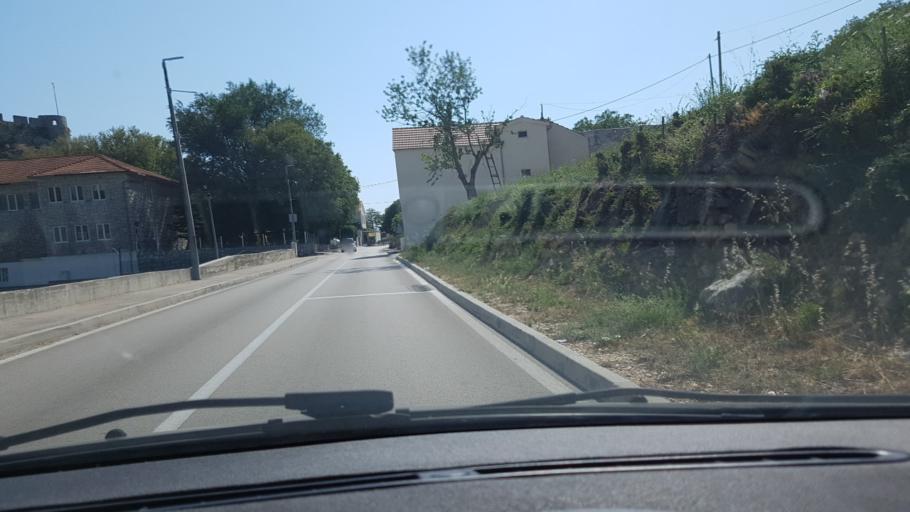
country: HR
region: Splitsko-Dalmatinska
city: Klis
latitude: 43.5618
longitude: 16.5237
